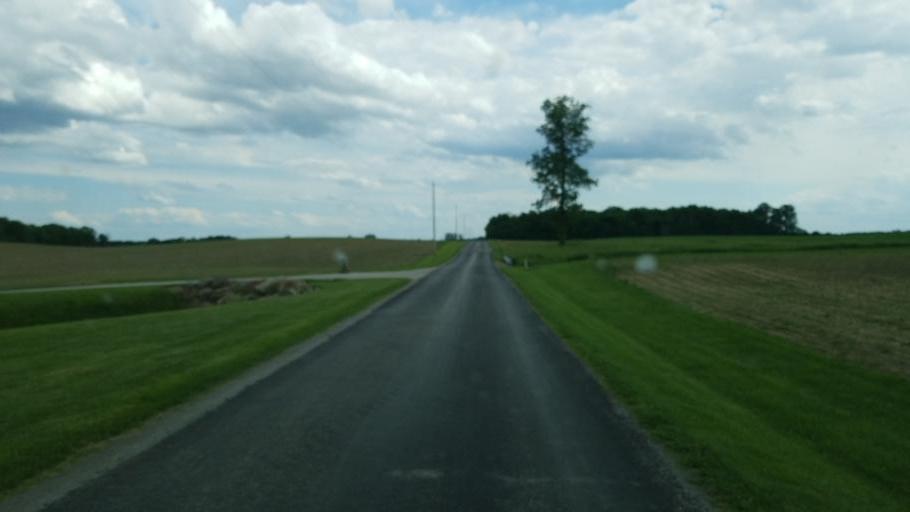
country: US
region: Ohio
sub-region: Richland County
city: Shelby
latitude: 40.9363
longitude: -82.5714
